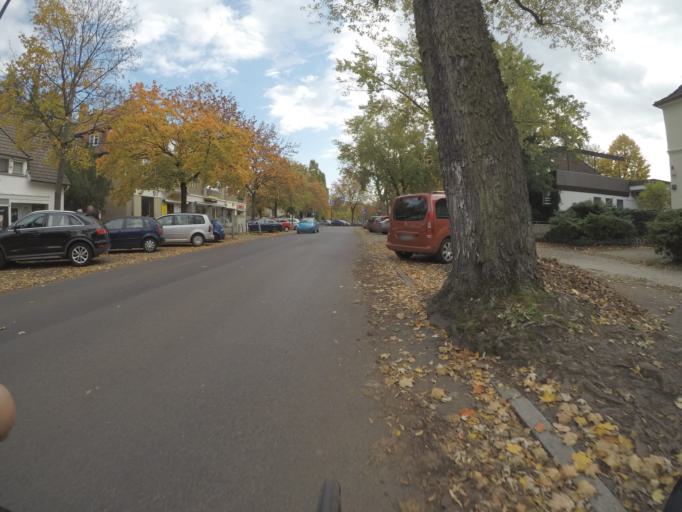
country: DE
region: Berlin
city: Frohnau
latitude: 52.6334
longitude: 13.2871
